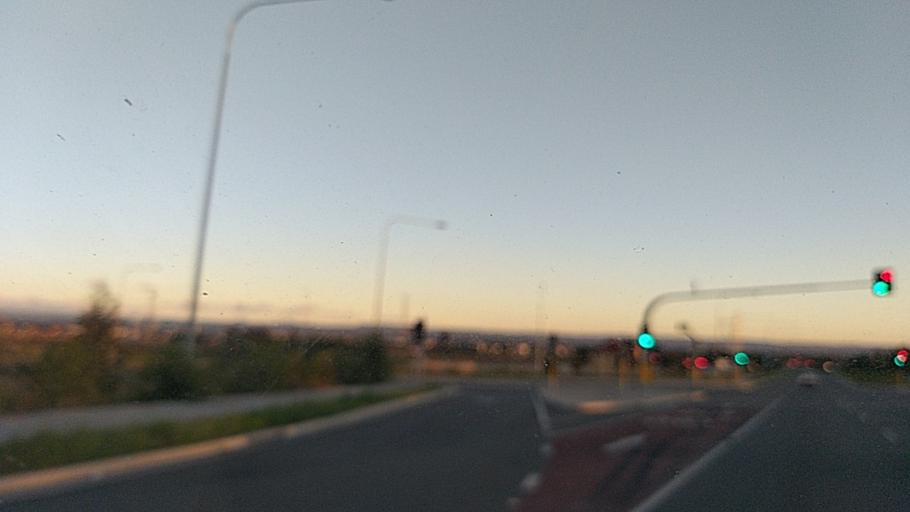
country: AU
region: New South Wales
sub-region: Blacktown
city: Hassall Grove
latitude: -33.6975
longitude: 150.8314
